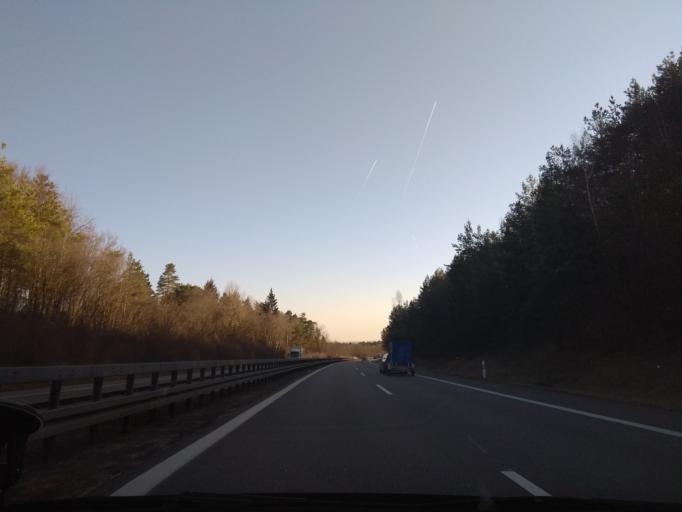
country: DE
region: Baden-Wuerttemberg
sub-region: Regierungsbezirk Stuttgart
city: Schlaitdorf
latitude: 48.6081
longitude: 9.2027
